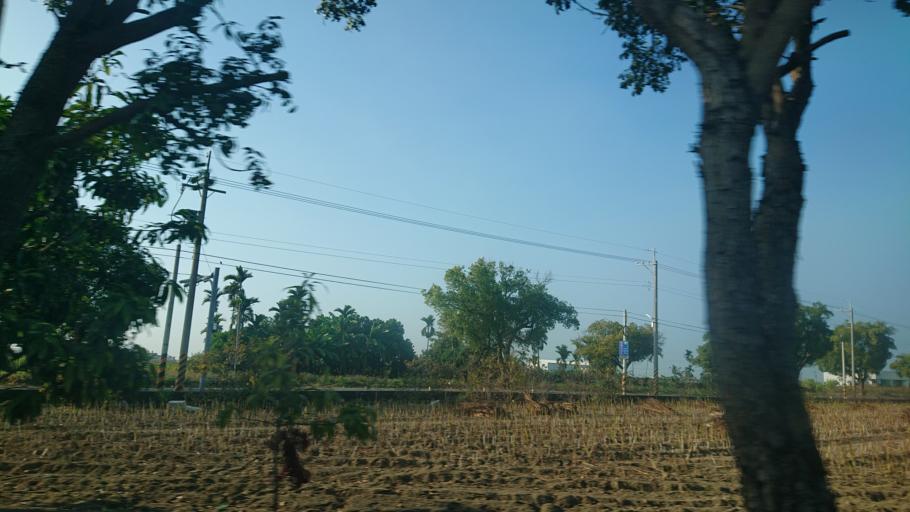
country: TW
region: Taiwan
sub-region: Tainan
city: Tainan
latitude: 23.1241
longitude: 120.2241
